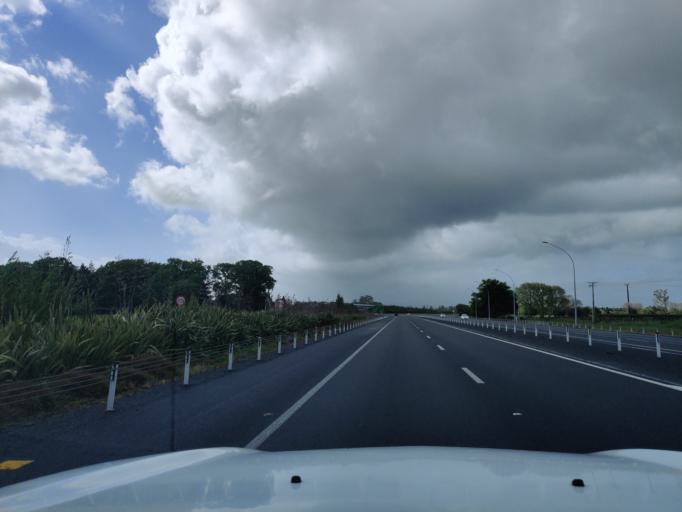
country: NZ
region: Waikato
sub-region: Waipa District
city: Cambridge
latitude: -37.8634
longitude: 175.4012
